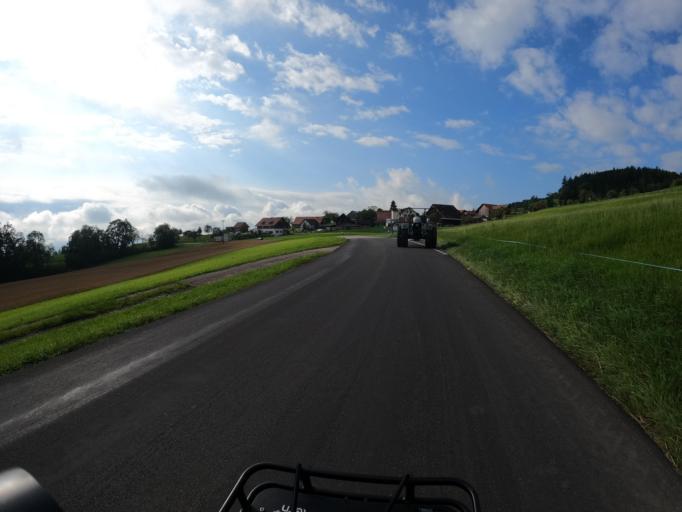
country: CH
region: Aargau
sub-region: Bezirk Muri
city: Buttwil
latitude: 47.2342
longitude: 8.3275
